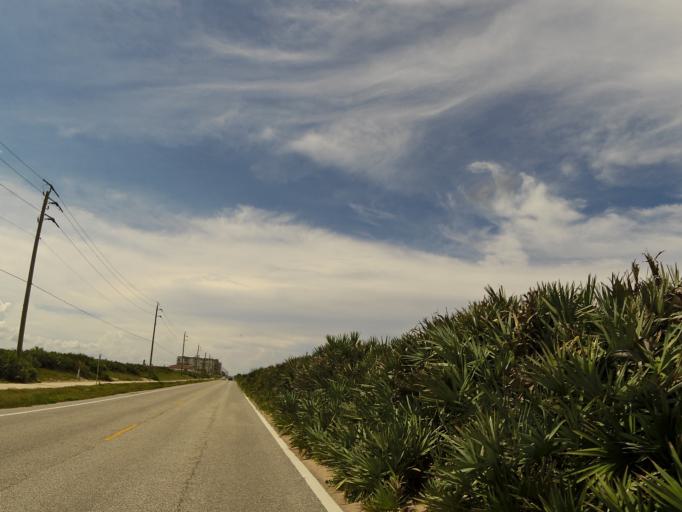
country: US
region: Florida
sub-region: Flagler County
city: Flagler Beach
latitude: 29.4243
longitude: -81.1014
